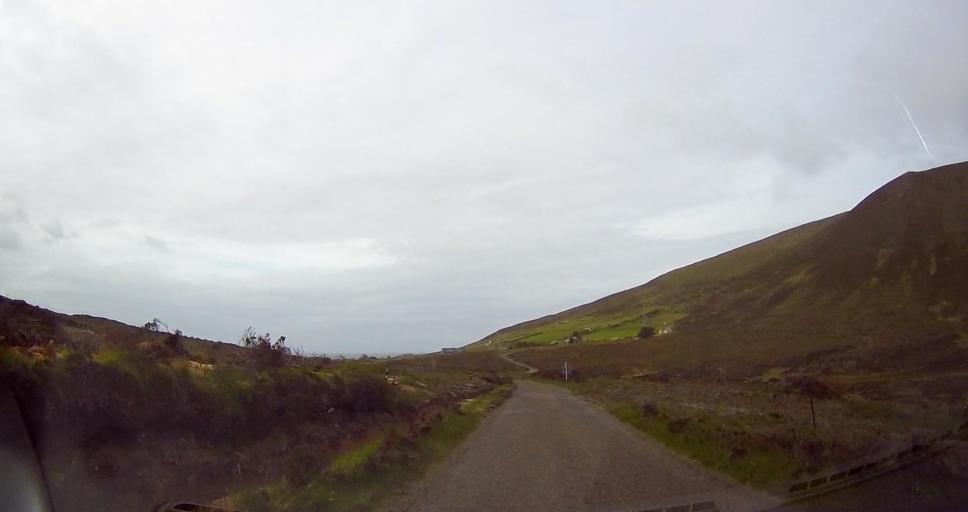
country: GB
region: Scotland
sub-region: Orkney Islands
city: Stromness
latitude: 58.8817
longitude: -3.3813
